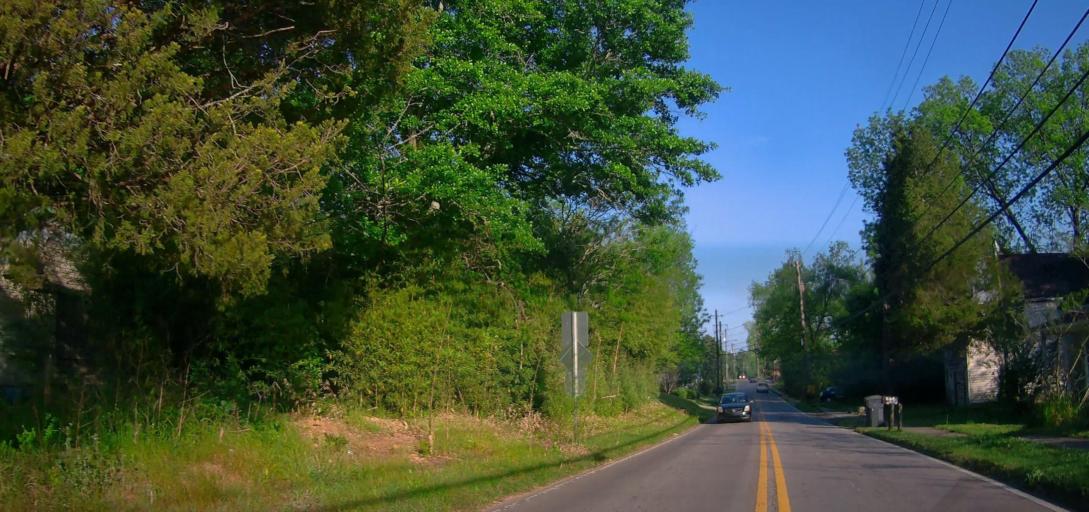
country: US
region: Georgia
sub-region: Putnam County
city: Eatonton
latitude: 33.3238
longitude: -83.3811
